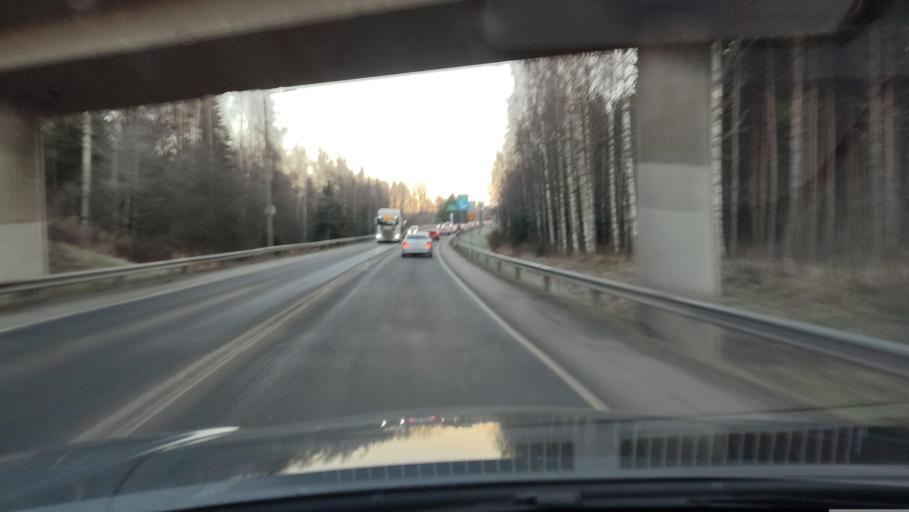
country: FI
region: Ostrobothnia
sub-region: Vaasa
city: Teeriniemi
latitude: 63.0774
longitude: 21.6845
